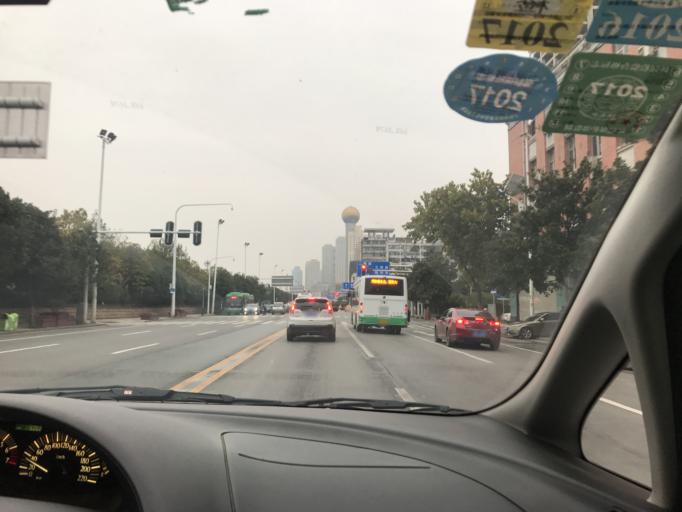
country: CN
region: Hubei
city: Jiang'an
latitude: 30.6016
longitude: 114.3039
